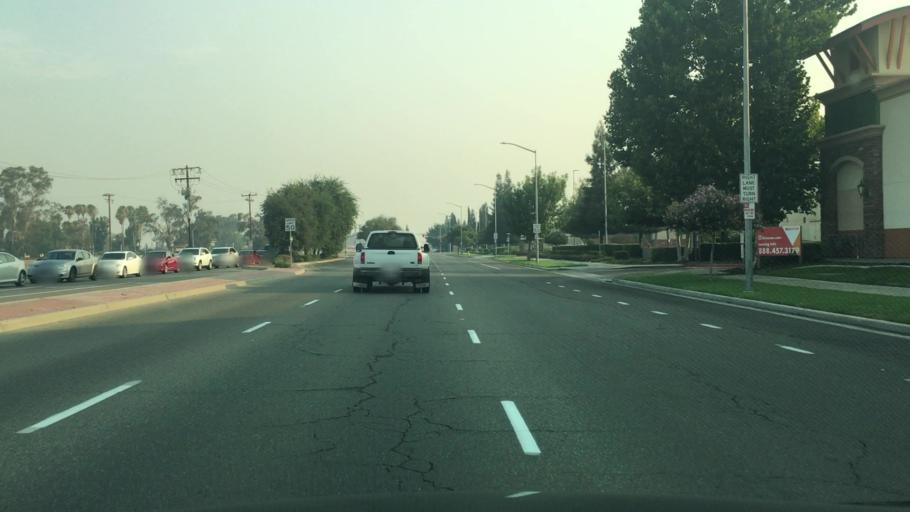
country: US
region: California
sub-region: Fresno County
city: Clovis
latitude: 36.8381
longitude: -119.7295
